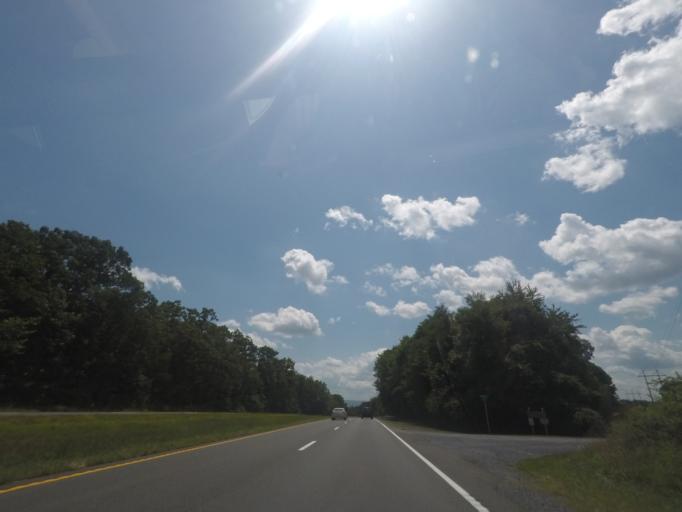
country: US
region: Virginia
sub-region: City of Winchester
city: Winchester
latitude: 39.1051
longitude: -78.1146
